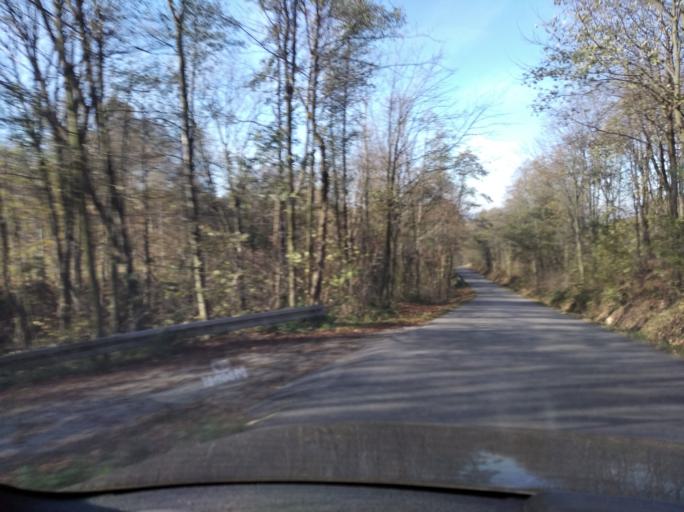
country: PL
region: Subcarpathian Voivodeship
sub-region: Powiat ropczycko-sedziszowski
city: Wielopole Skrzynskie
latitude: 49.8995
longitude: 21.5743
